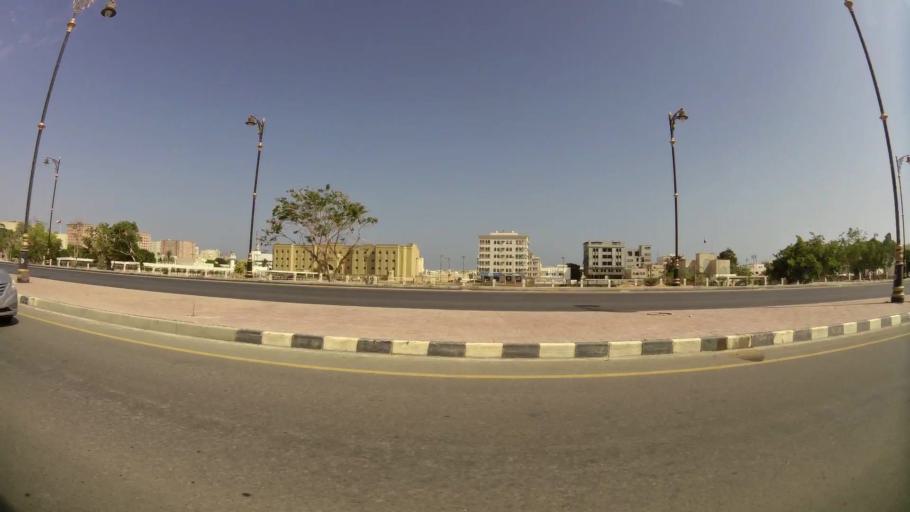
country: OM
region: Zufar
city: Salalah
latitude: 17.0238
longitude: 54.0877
